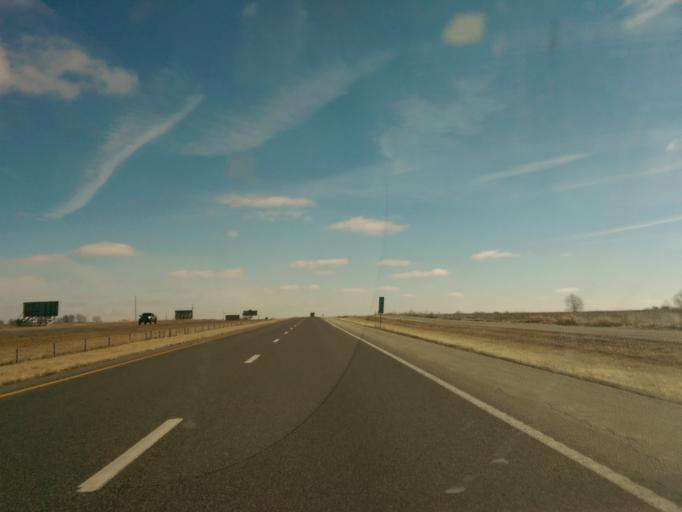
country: US
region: Missouri
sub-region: Callaway County
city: Fulton
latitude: 38.9424
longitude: -91.8762
